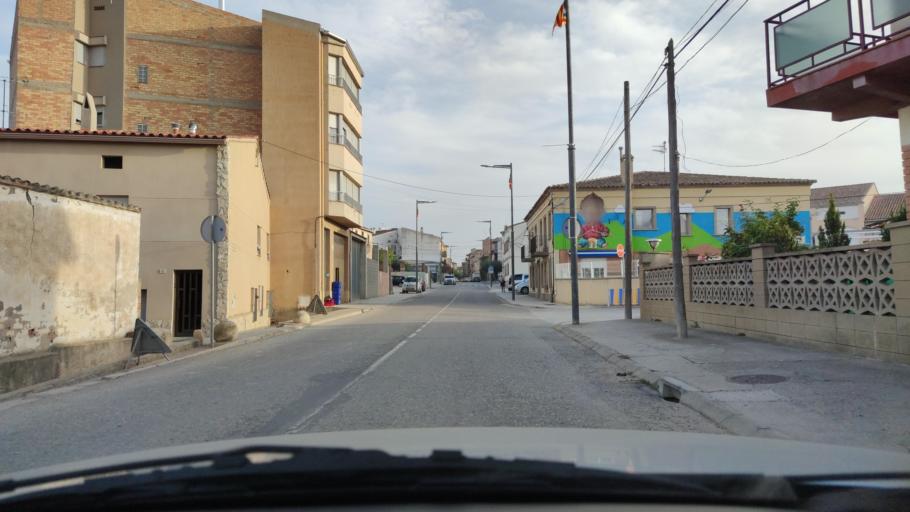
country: ES
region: Catalonia
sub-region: Provincia de Lleida
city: Anglesola
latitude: 41.6560
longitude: 1.0823
